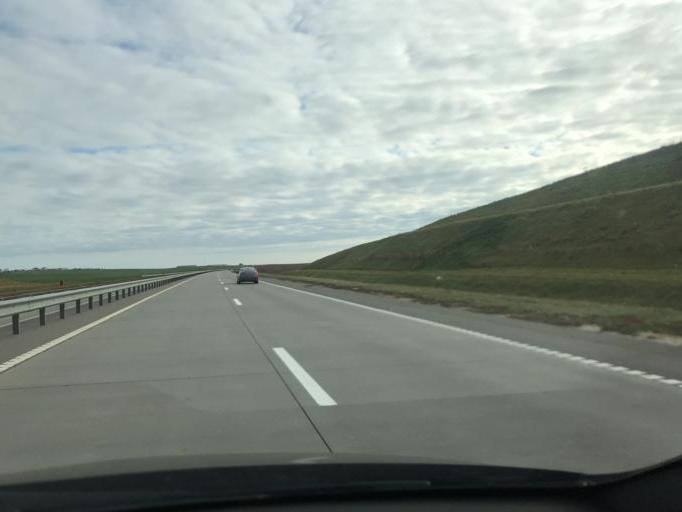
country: BY
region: Minsk
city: Syomkava
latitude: 54.0675
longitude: 27.4709
